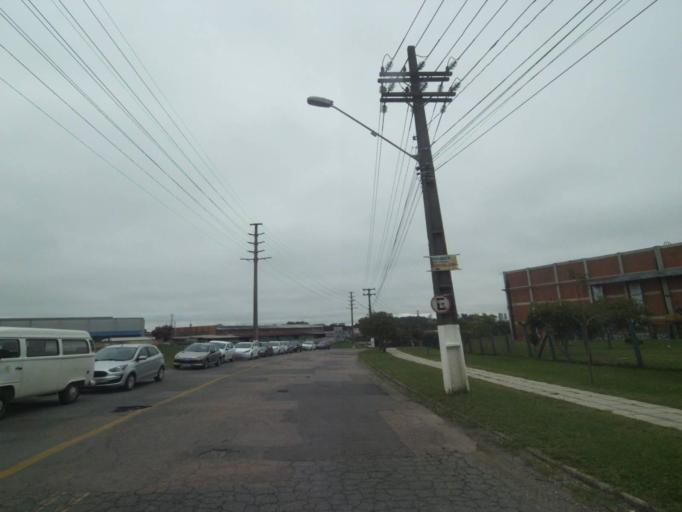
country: BR
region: Parana
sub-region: Sao Jose Dos Pinhais
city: Sao Jose dos Pinhais
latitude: -25.5406
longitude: -49.3126
